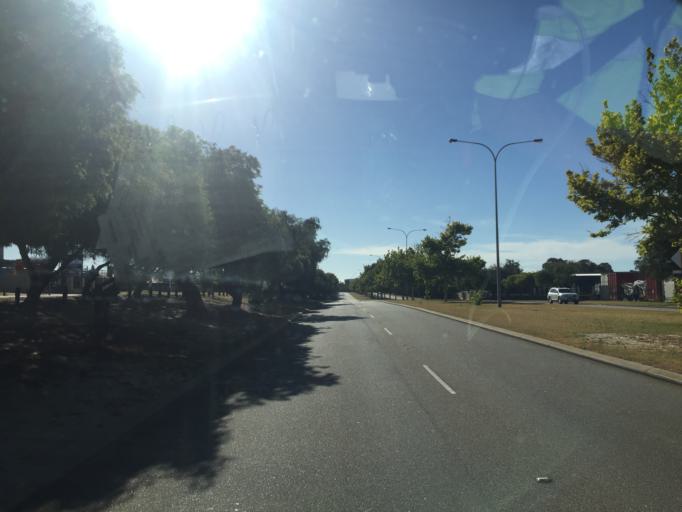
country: AU
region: Western Australia
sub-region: Canning
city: Queens Park
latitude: -31.9956
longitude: 115.9540
